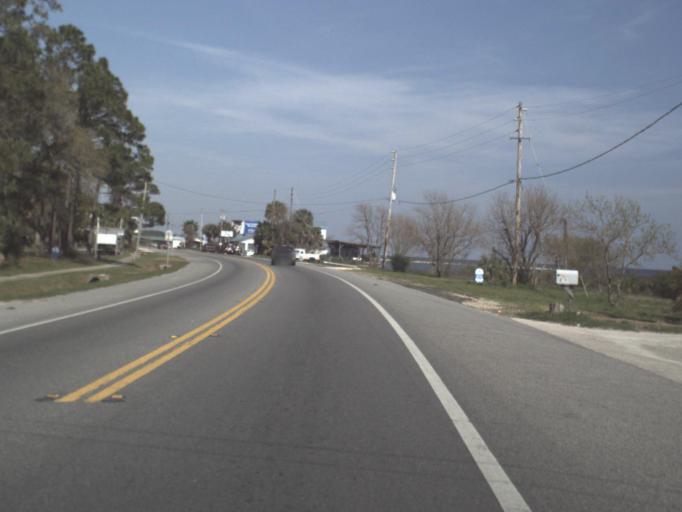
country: US
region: Florida
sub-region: Franklin County
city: Eastpoint
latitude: 29.7369
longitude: -84.8779
